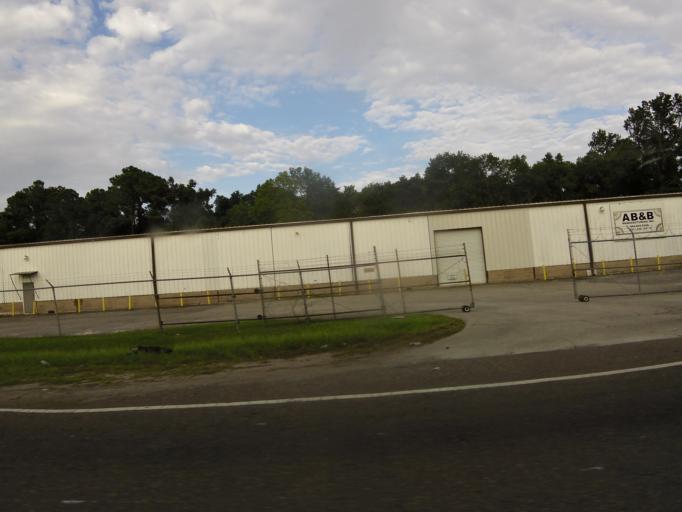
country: US
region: Florida
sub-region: Duval County
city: Jacksonville
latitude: 30.3494
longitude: -81.7521
